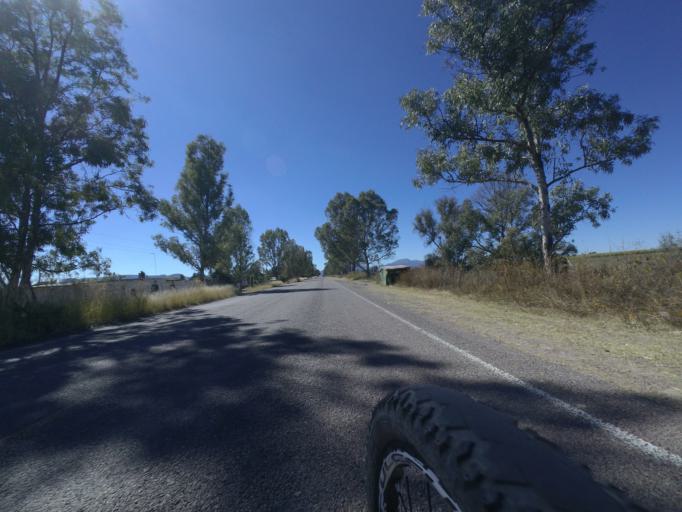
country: MX
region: Aguascalientes
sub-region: Aguascalientes
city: Los Canos
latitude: 21.8754
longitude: -102.4953
